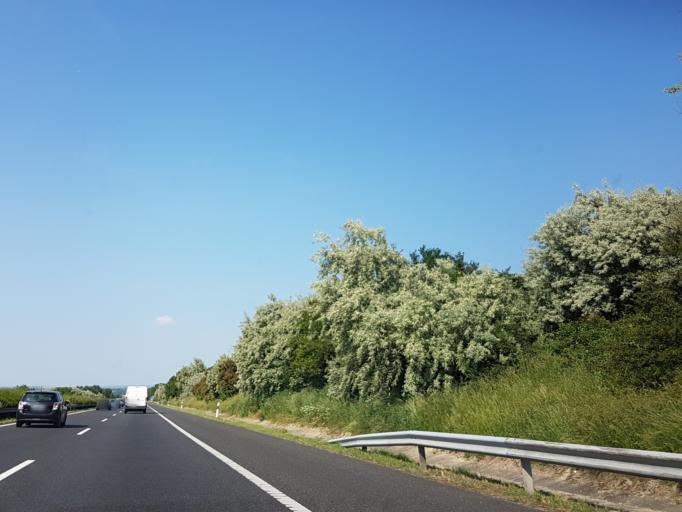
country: HU
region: Fejer
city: Szabadbattyan
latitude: 47.0881
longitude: 18.3621
